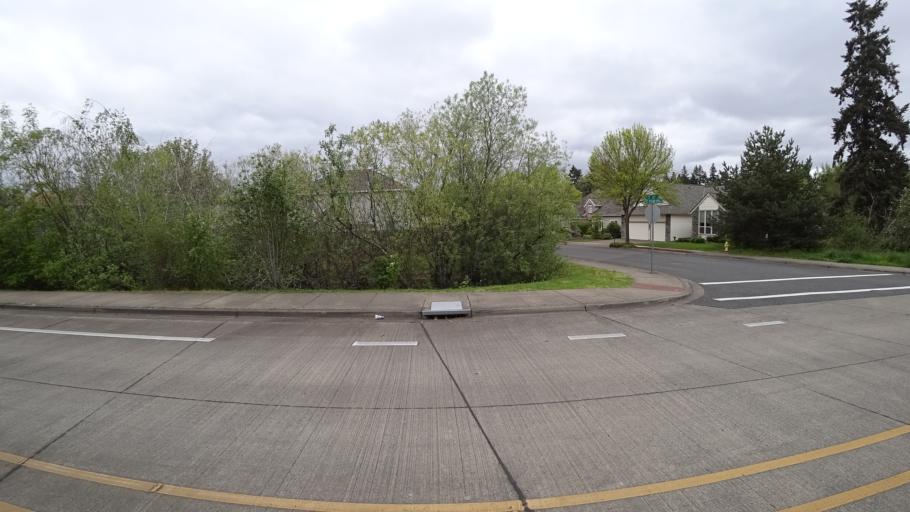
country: US
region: Oregon
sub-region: Washington County
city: Beaverton
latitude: 45.4584
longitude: -122.8351
